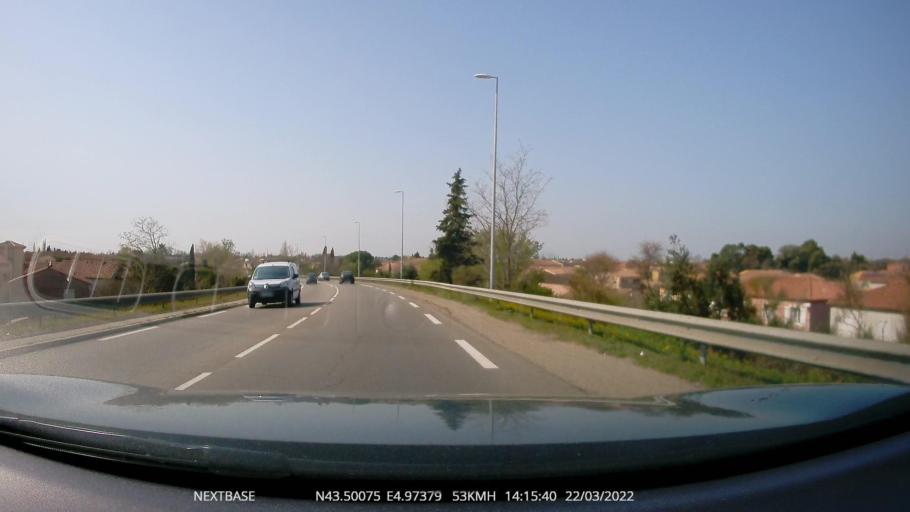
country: FR
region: Provence-Alpes-Cote d'Azur
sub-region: Departement des Bouches-du-Rhone
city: Istres
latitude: 43.5006
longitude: 4.9741
